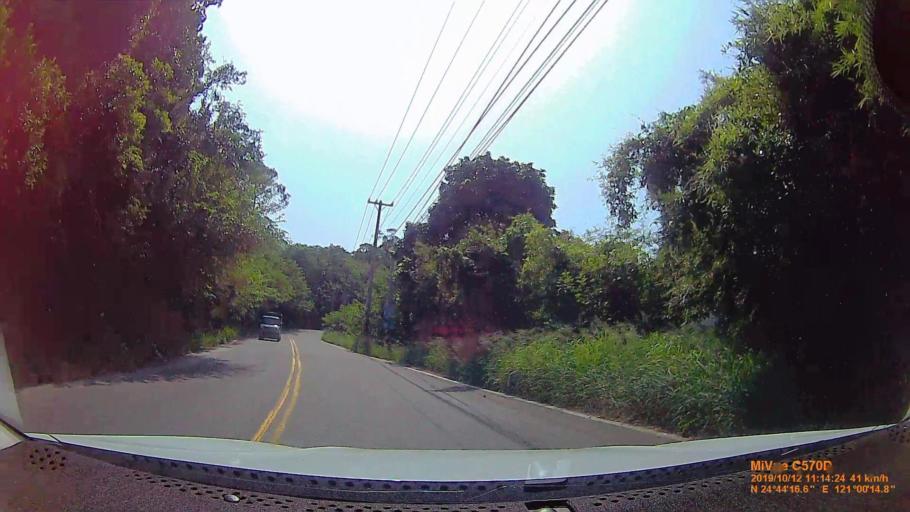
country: TW
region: Taiwan
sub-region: Hsinchu
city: Hsinchu
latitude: 24.7378
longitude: 121.0043
